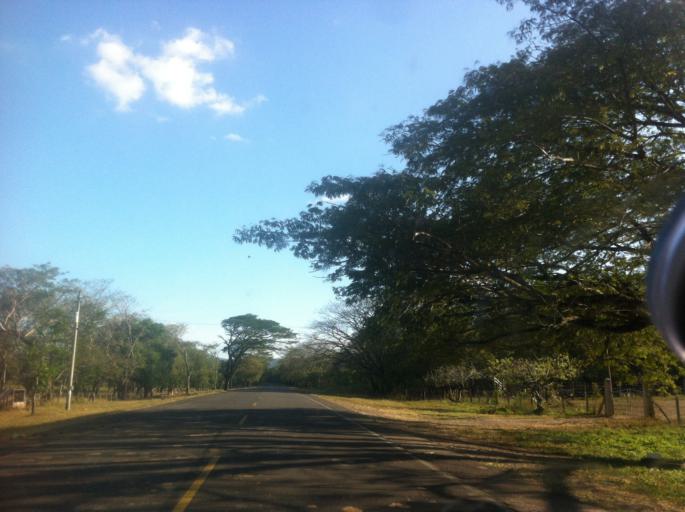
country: NI
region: Rio San Juan
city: Morrito
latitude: 11.8173
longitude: -85.0349
